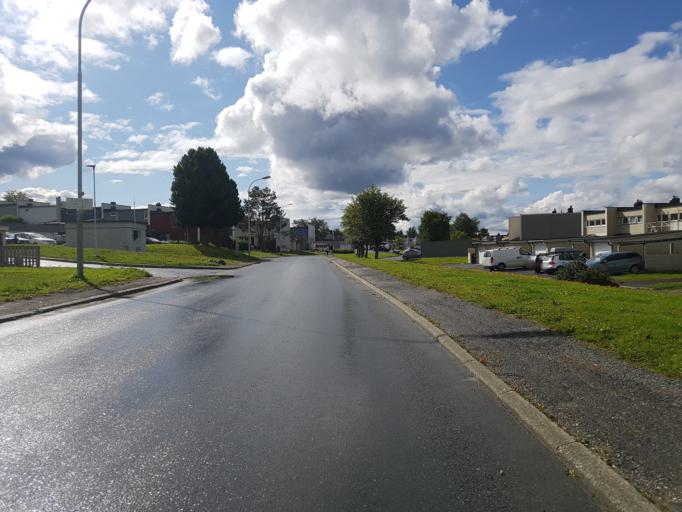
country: NO
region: Sor-Trondelag
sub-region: Trondheim
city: Trondheim
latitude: 63.4141
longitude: 10.4611
